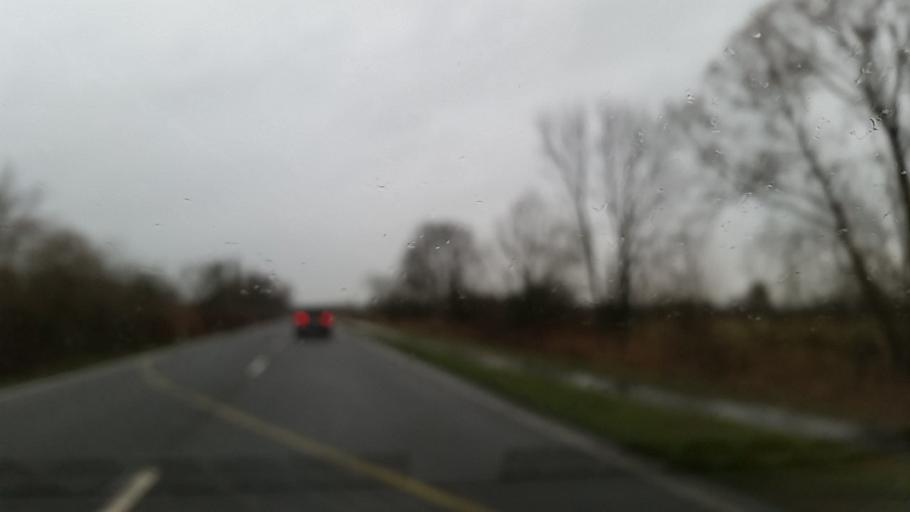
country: DE
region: Brandenburg
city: Friesack
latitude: 52.7734
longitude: 12.5615
